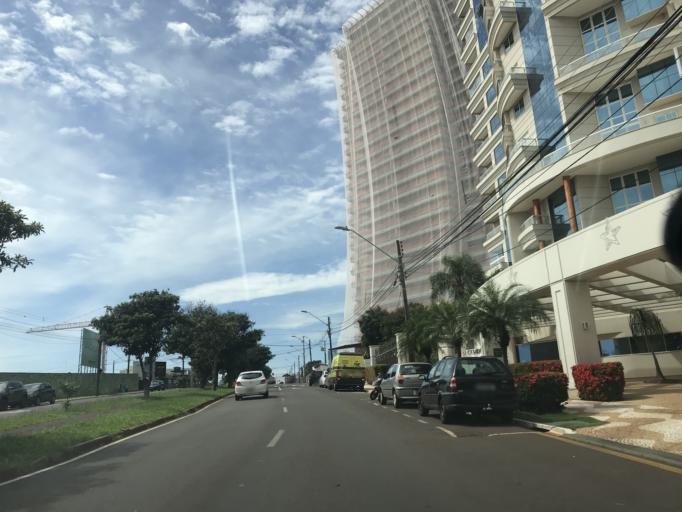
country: BR
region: Parana
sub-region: Londrina
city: Londrina
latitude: -23.3416
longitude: -51.1644
